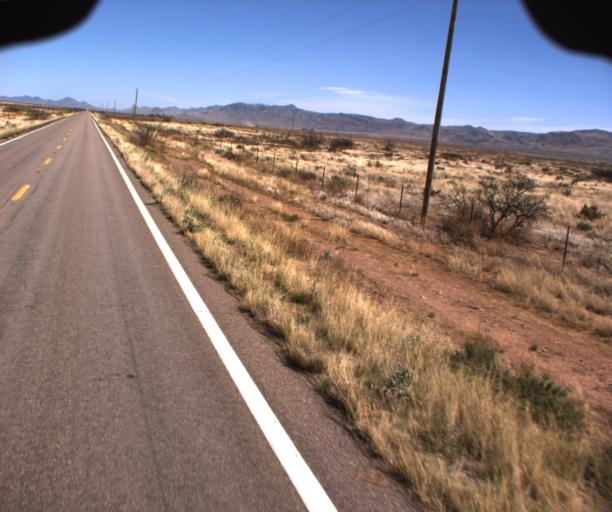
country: US
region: Arizona
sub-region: Cochise County
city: Douglas
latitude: 31.7167
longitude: -109.1146
